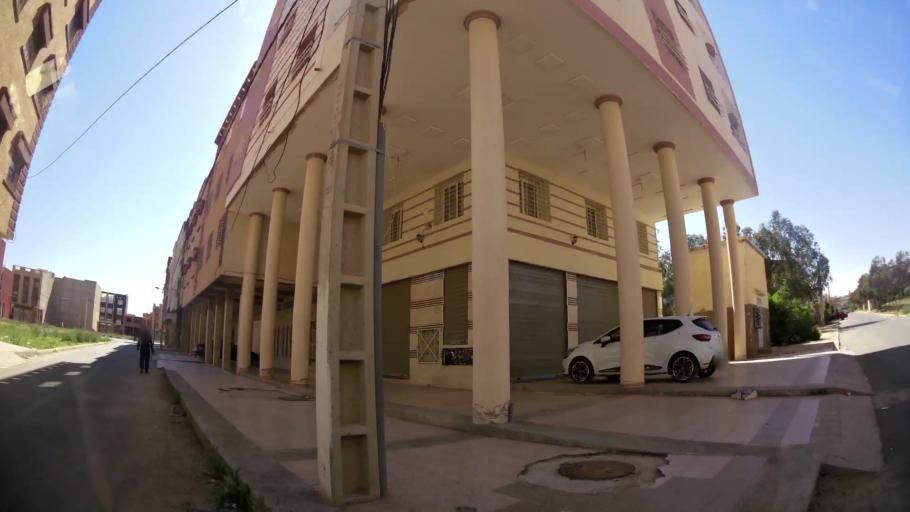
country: MA
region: Oriental
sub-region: Oujda-Angad
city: Oujda
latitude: 34.6600
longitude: -1.8875
